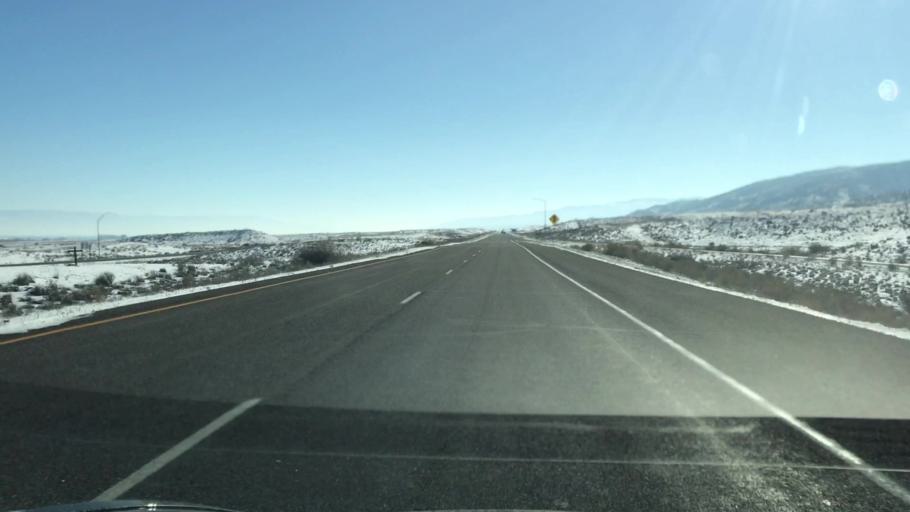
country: US
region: Colorado
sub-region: Mesa County
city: Loma
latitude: 39.2121
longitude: -108.8665
